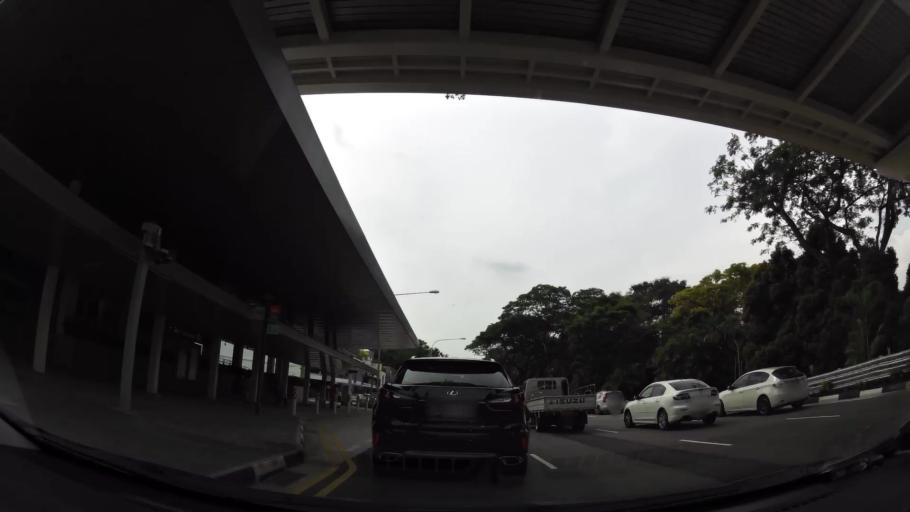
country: SG
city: Singapore
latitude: 1.3310
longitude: 103.7969
